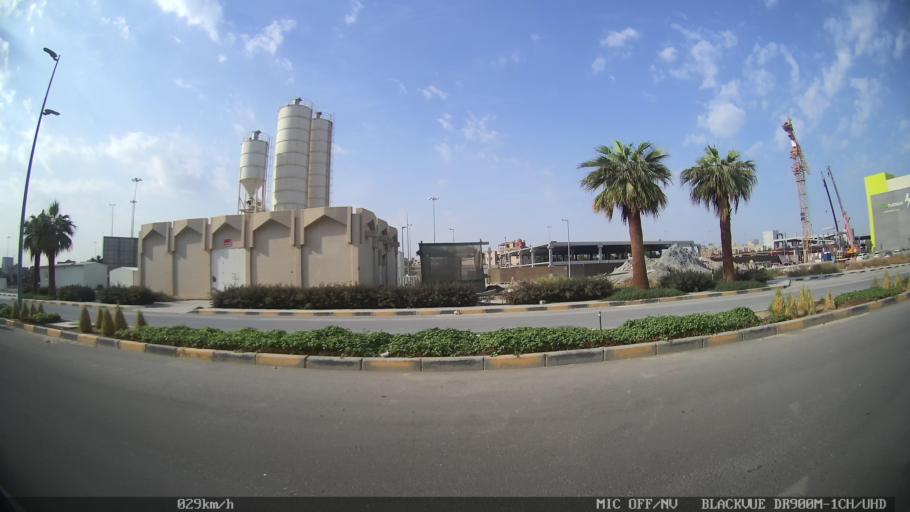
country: KW
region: Al Asimah
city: Ad Dasmah
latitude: 29.3594
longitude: 48.0214
